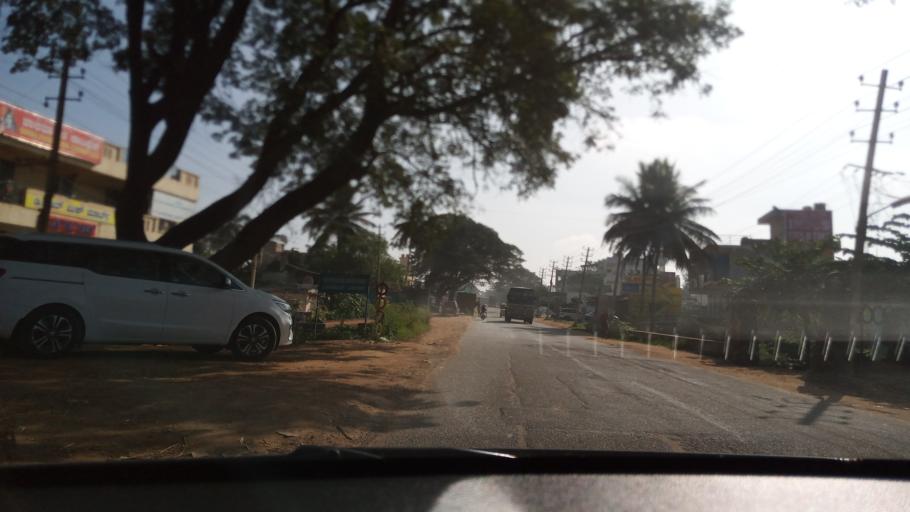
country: IN
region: Karnataka
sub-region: Bangalore Rural
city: Devanhalli
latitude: 13.2573
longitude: 77.7147
